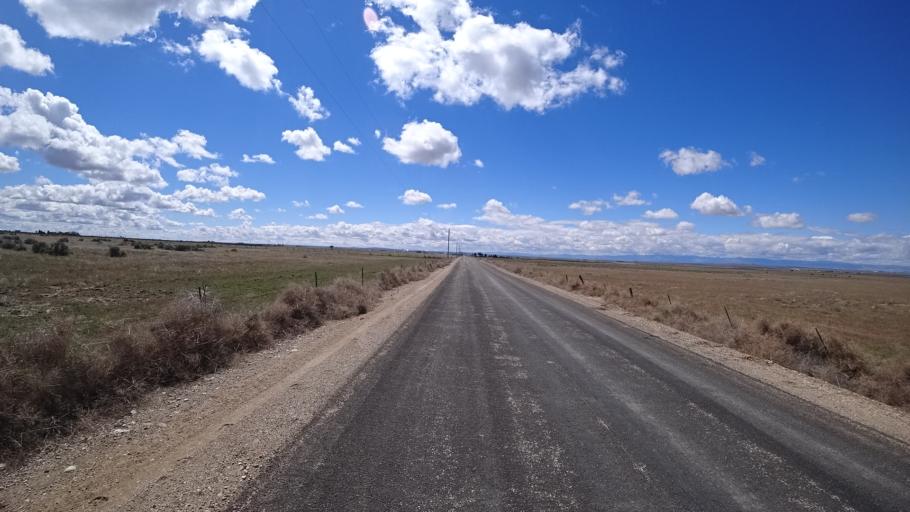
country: US
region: Idaho
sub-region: Ada County
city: Kuna
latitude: 43.4677
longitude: -116.2744
